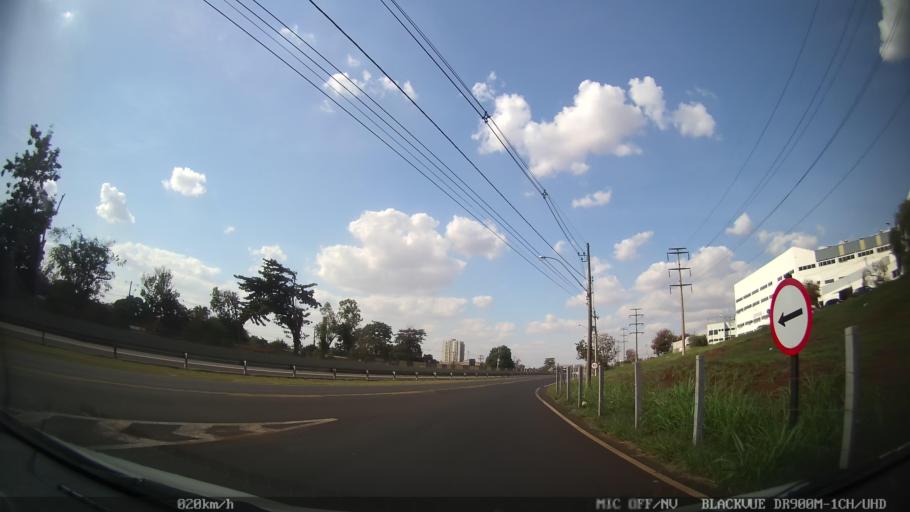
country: BR
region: Sao Paulo
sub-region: Ribeirao Preto
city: Ribeirao Preto
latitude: -21.1792
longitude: -47.8374
